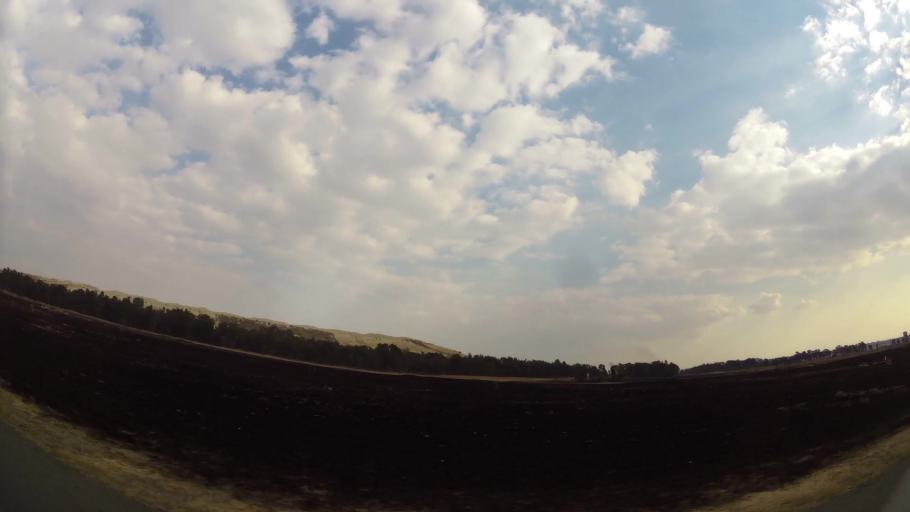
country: ZA
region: Gauteng
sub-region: Ekurhuleni Metropolitan Municipality
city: Springs
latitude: -26.2847
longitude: 28.5314
